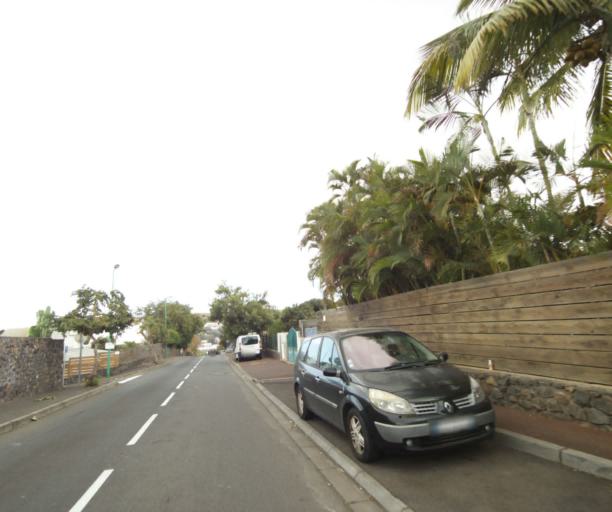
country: RE
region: Reunion
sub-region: Reunion
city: Saint-Paul
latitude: -21.0580
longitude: 55.2273
